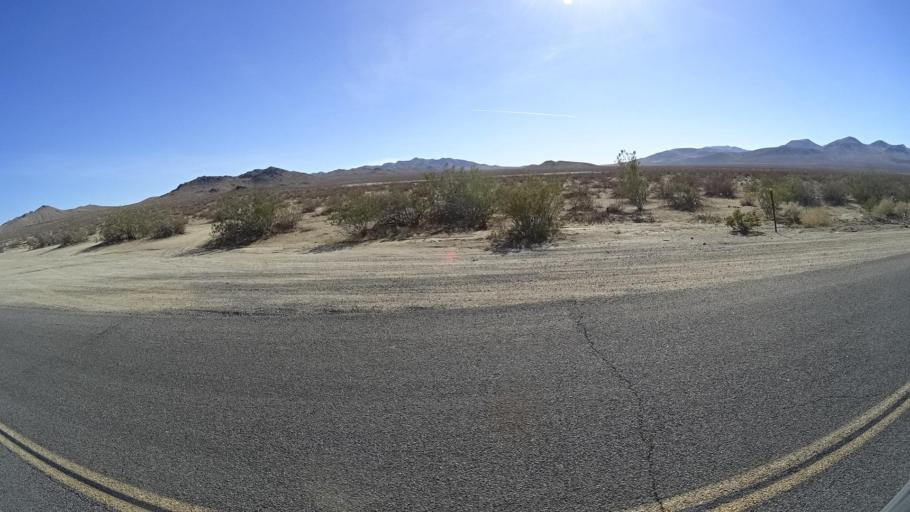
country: US
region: California
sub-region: Kern County
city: Ridgecrest
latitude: 35.5500
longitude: -117.7158
